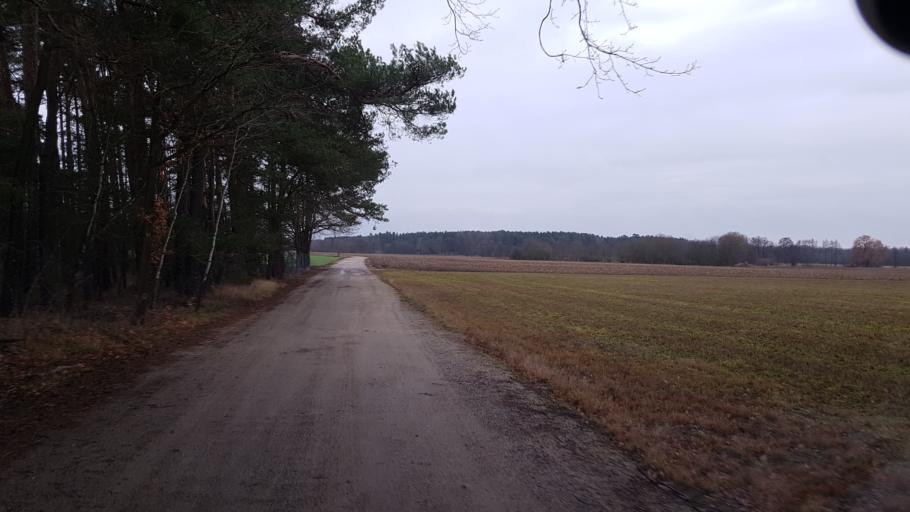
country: DE
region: Brandenburg
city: Altdobern
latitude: 51.6903
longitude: 14.0449
